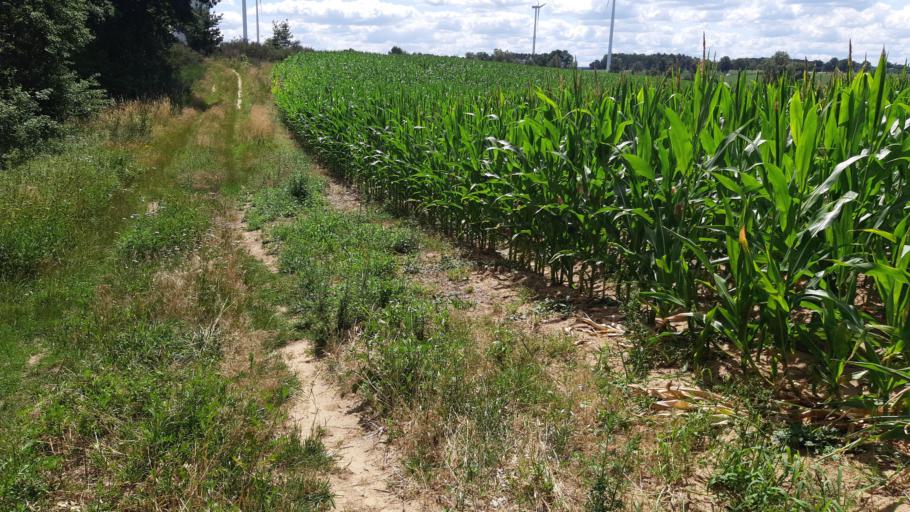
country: DE
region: Lower Saxony
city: Dahlem
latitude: 53.1954
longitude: 10.7787
